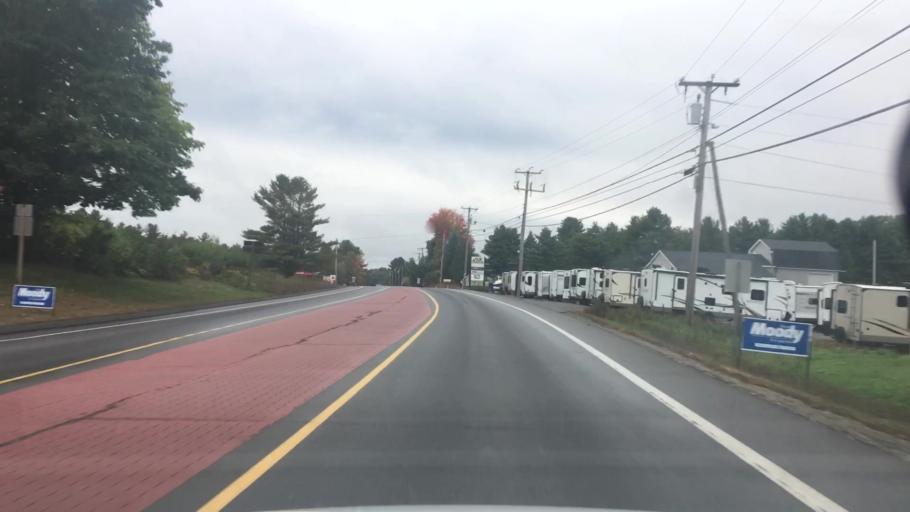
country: US
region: Maine
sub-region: Kennebec County
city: Augusta
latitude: 44.3729
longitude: -69.7944
